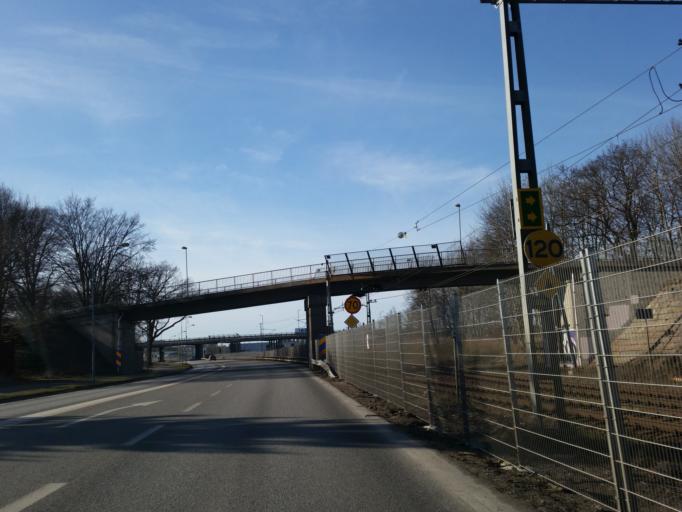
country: SE
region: Kalmar
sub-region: Kalmar Kommun
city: Kalmar
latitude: 56.6696
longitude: 16.3210
